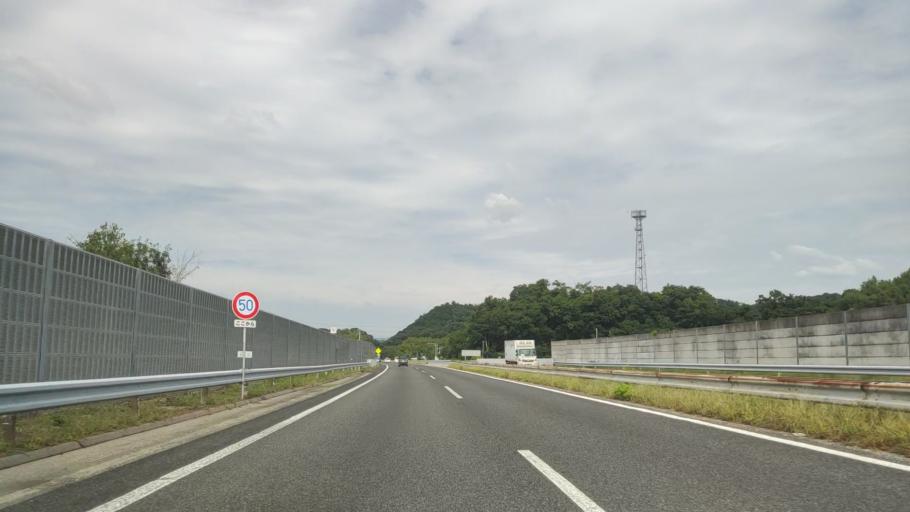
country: JP
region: Wakayama
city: Kainan
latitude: 34.1737
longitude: 135.2356
